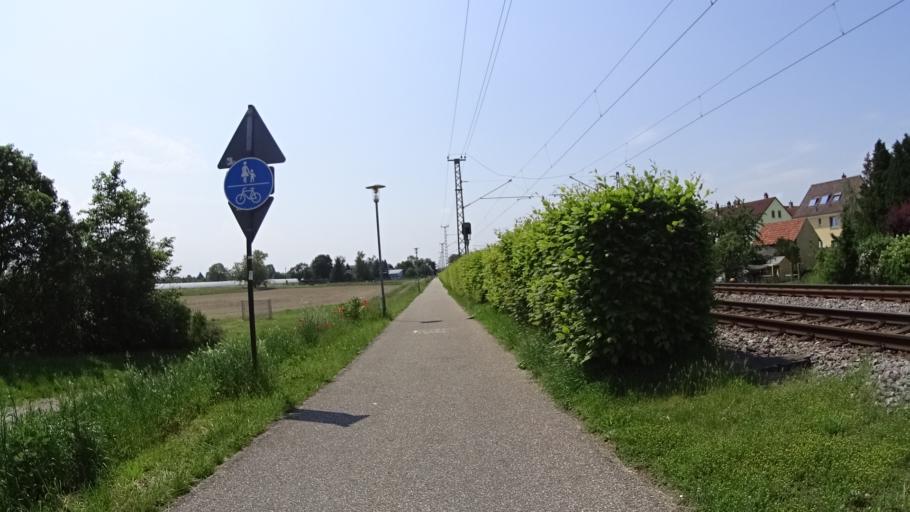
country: DE
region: Baden-Wuerttemberg
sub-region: Karlsruhe Region
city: Eggenstein-Leopoldshafen
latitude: 49.0794
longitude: 8.3996
